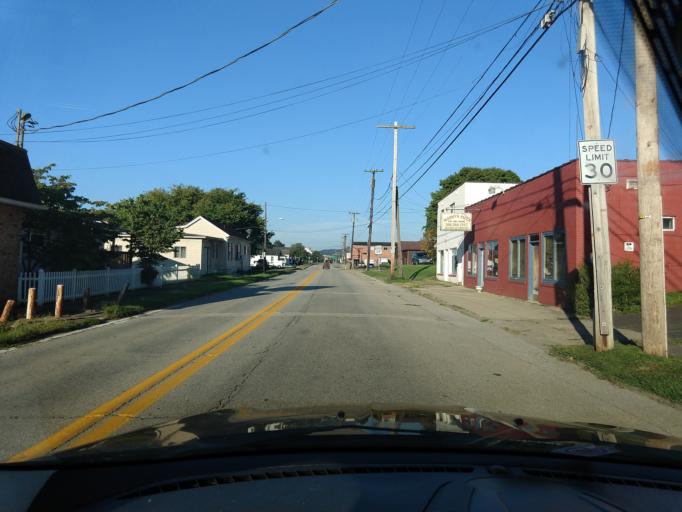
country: US
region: West Virginia
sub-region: Kanawha County
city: Charleston
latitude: 38.3641
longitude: -81.6137
